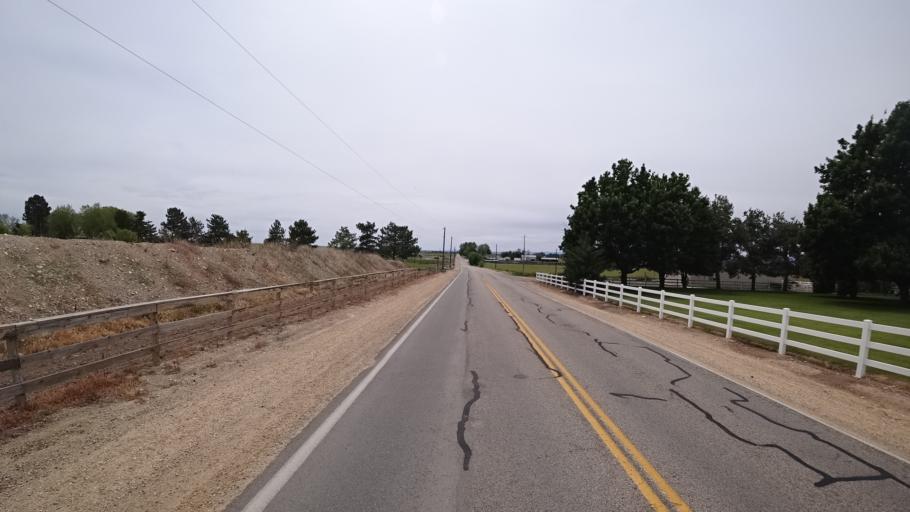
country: US
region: Idaho
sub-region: Ada County
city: Meridian
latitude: 43.5545
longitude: -116.3747
